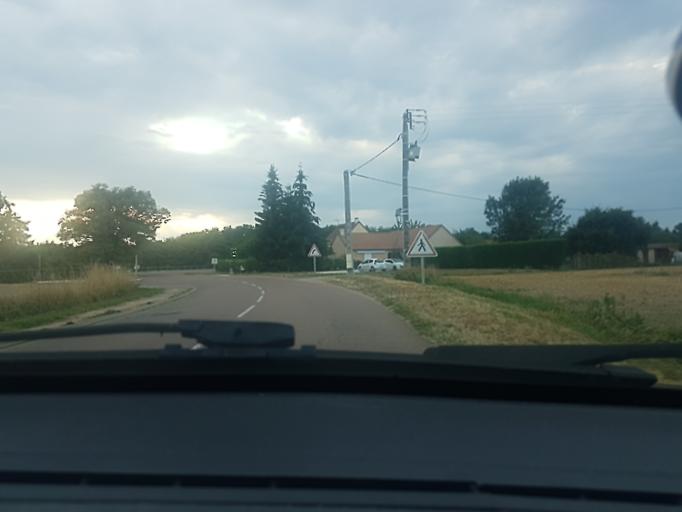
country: FR
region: Bourgogne
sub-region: Departement de Saone-et-Loire
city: Buxy
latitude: 46.7293
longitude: 4.7504
